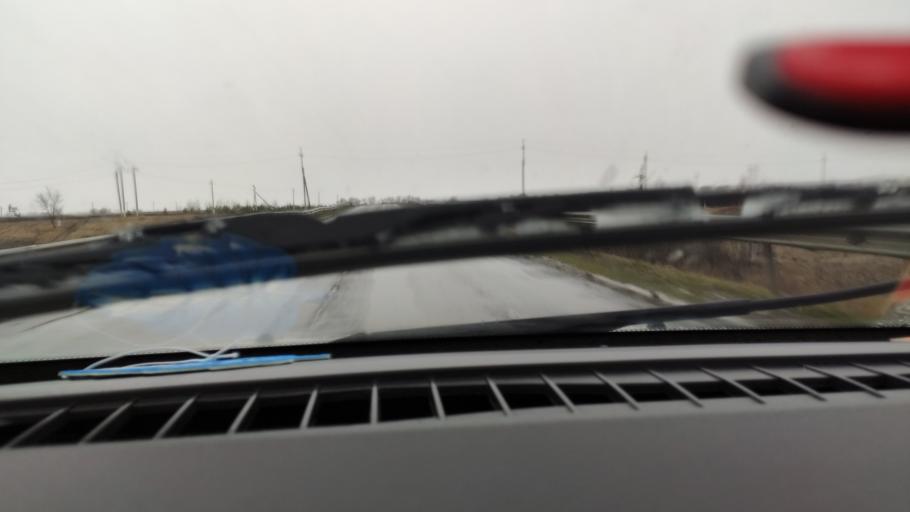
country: RU
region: Samara
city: Chelno-Vershiny
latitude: 54.7073
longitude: 51.1758
